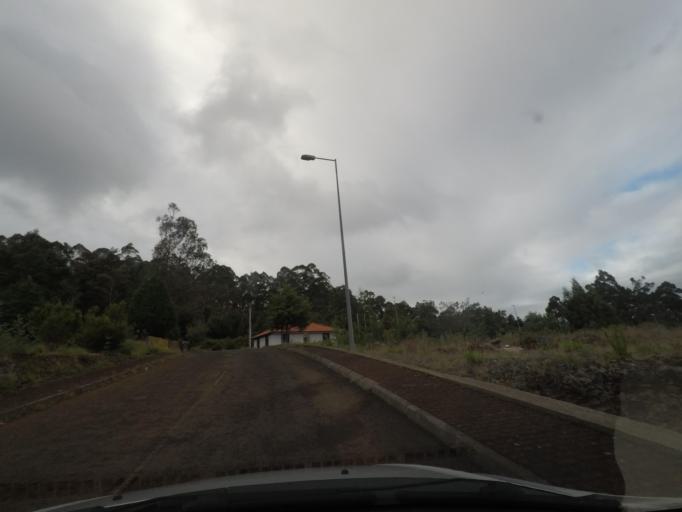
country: PT
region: Madeira
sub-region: Santana
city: Santana
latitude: 32.7860
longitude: -16.8798
